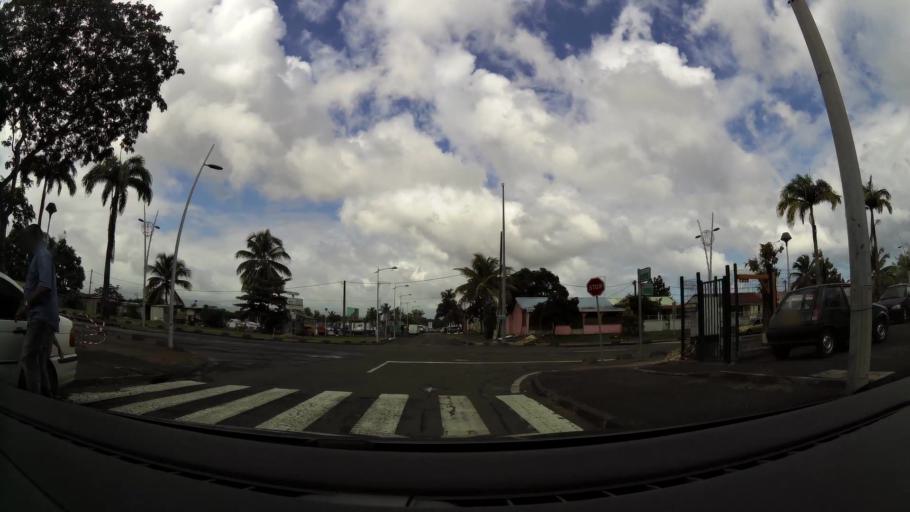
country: GP
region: Guadeloupe
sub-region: Guadeloupe
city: Pointe-a-Pitre
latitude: 16.2507
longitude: -61.5469
